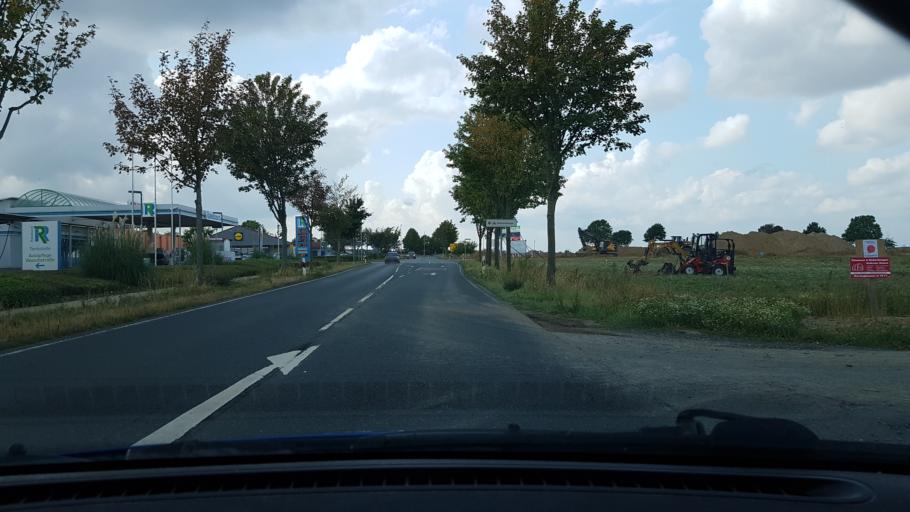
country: DE
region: Lower Saxony
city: Barsinghausen
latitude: 52.3164
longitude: 9.4680
